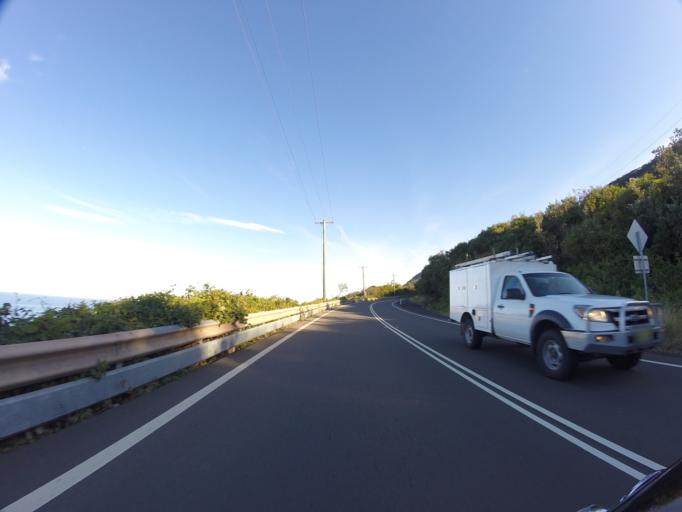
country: AU
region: New South Wales
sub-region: Wollongong
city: Helensburgh
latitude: -34.2362
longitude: 150.9855
